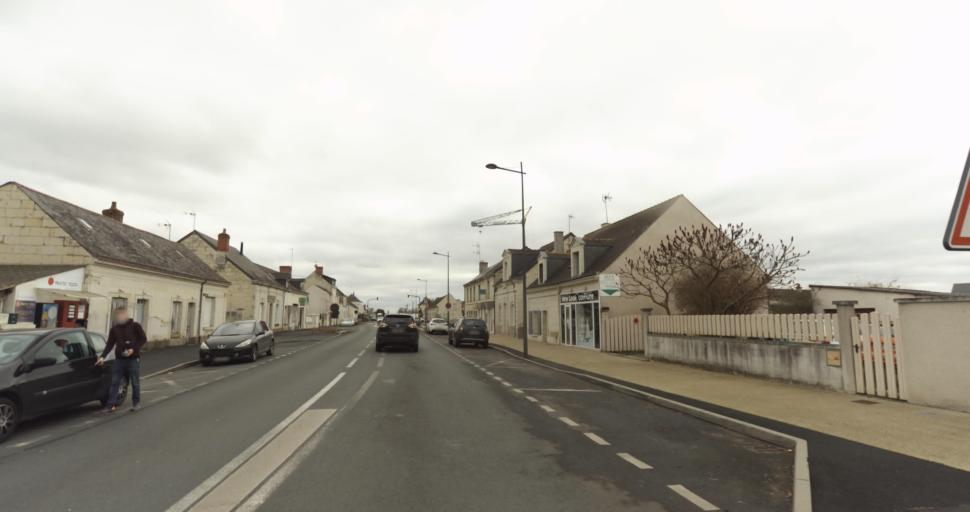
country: FR
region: Pays de la Loire
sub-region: Departement de Maine-et-Loire
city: Vivy
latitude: 47.3249
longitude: -0.0551
